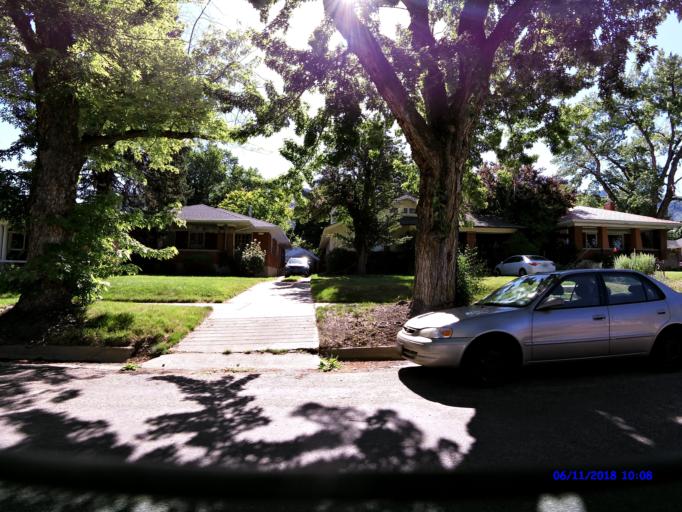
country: US
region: Utah
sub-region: Weber County
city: Ogden
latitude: 41.2187
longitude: -111.9455
